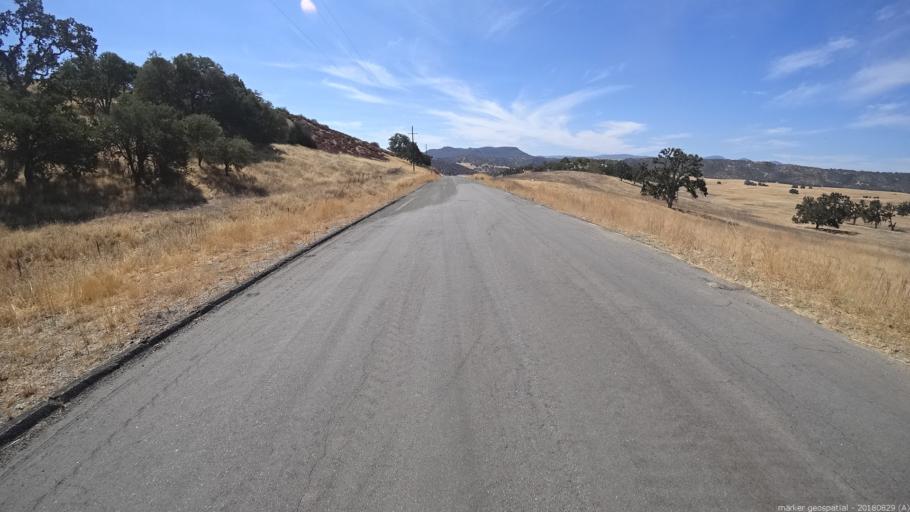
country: US
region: California
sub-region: San Luis Obispo County
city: Lake Nacimiento
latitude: 35.8261
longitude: -120.9807
